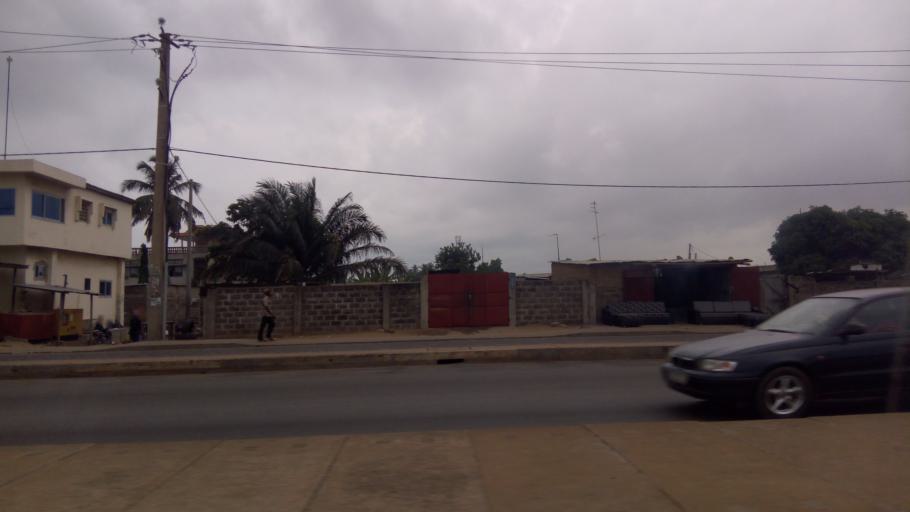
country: BJ
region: Atlantique
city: Abomey-Calavi
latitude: 6.3888
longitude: 2.3620
